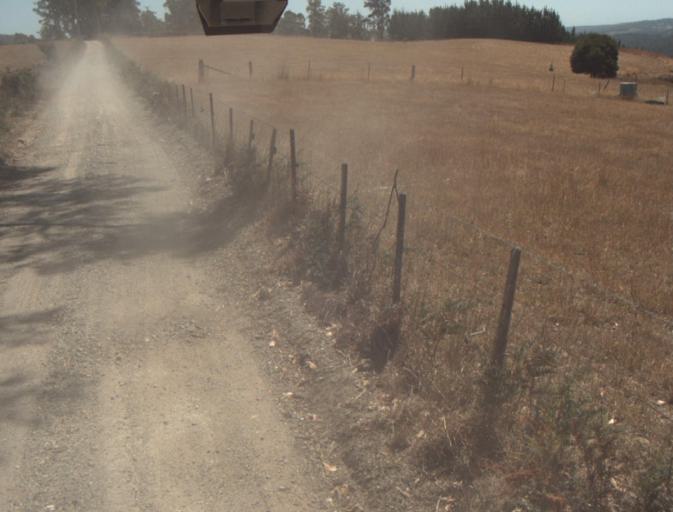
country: AU
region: Tasmania
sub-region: Launceston
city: Mayfield
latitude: -41.2430
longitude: 147.1300
